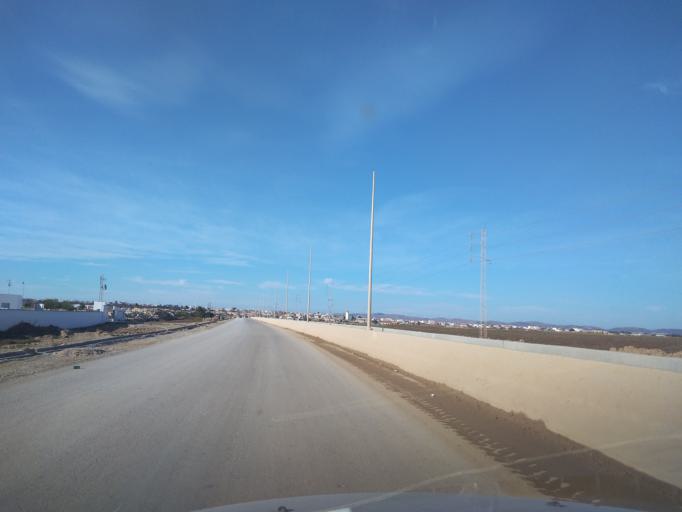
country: TN
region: Ariana
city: Qal'at al Andalus
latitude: 37.0398
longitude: 10.1315
